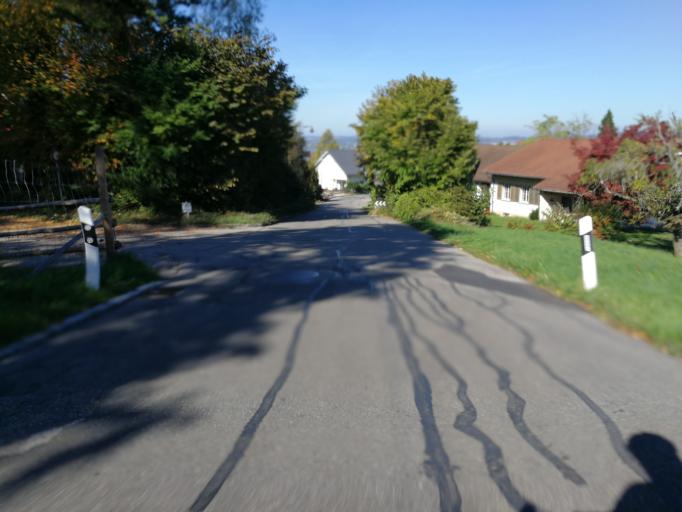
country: CH
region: Zurich
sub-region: Bezirk Uster
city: Aesch
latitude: 47.3360
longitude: 8.6686
